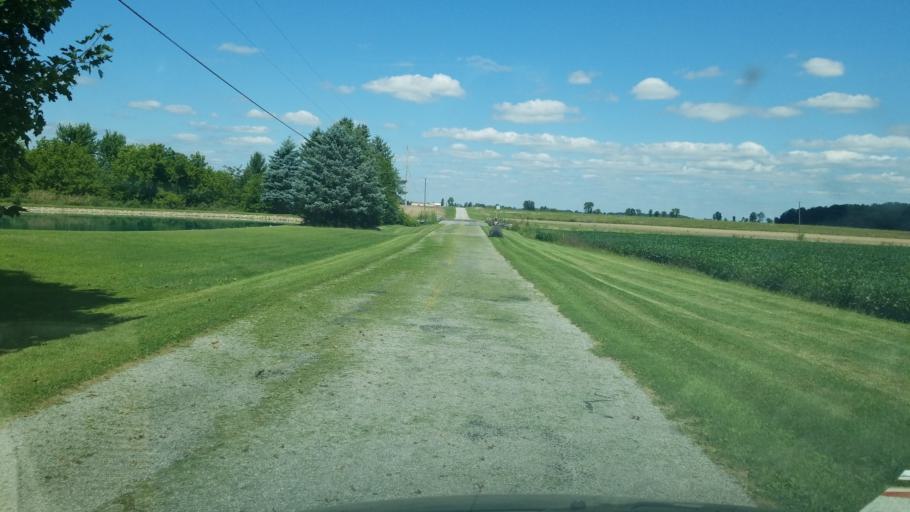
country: US
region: Ohio
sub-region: Fulton County
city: Delta
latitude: 41.7132
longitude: -84.0178
